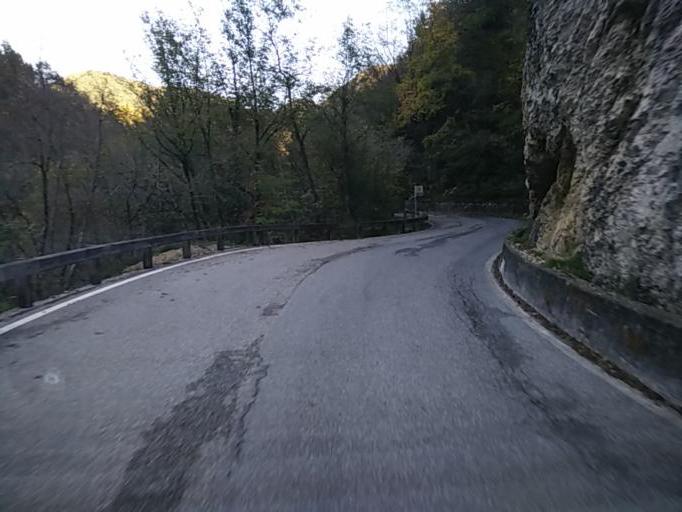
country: IT
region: Lombardy
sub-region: Provincia di Brescia
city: Gargnano
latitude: 45.7050
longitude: 10.6142
